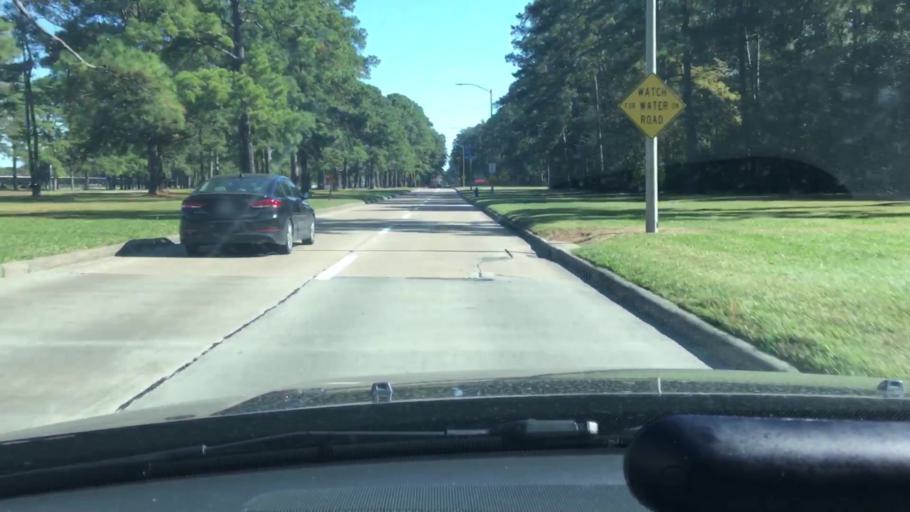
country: US
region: Texas
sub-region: Harris County
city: Humble
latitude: 29.9848
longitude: -95.3175
